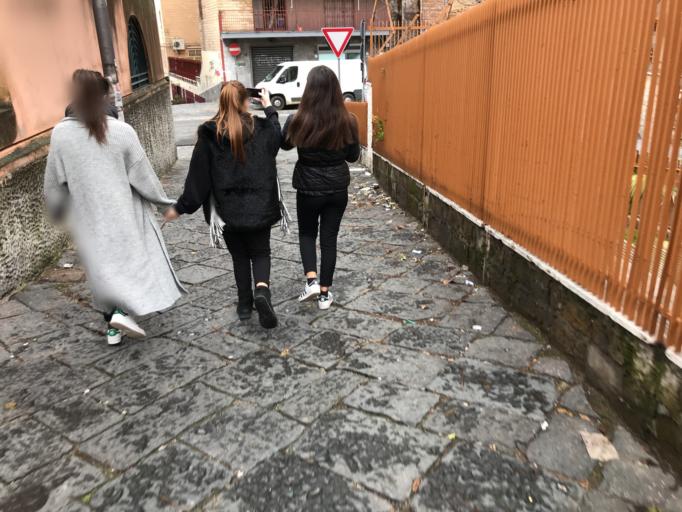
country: IT
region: Campania
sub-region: Provincia di Napoli
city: Napoli
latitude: 40.8556
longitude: 14.2298
